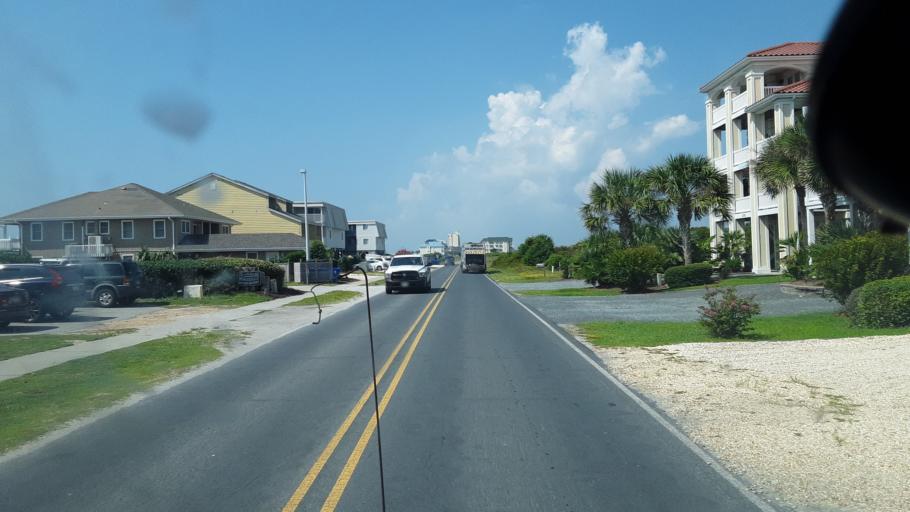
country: US
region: North Carolina
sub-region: Brunswick County
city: Sunset Beach
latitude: 33.8827
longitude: -78.4556
